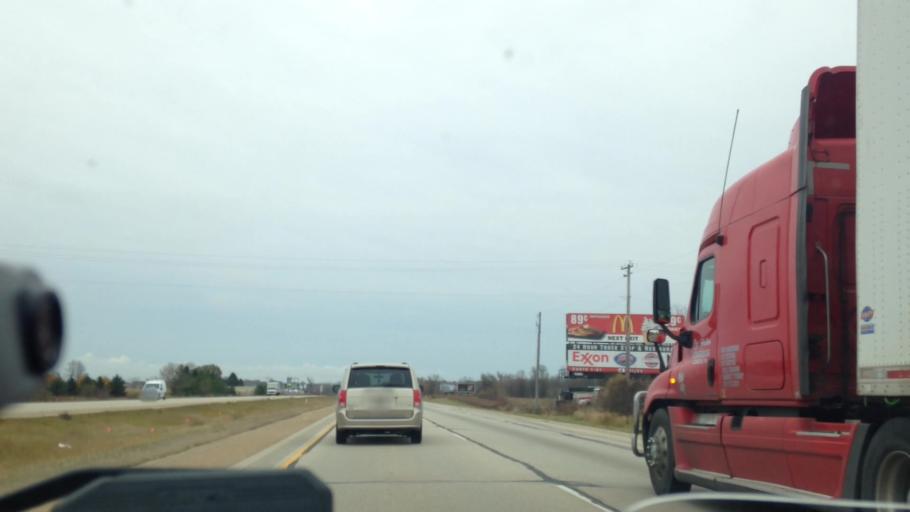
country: US
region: Wisconsin
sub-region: Washington County
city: Richfield
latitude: 43.3081
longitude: -88.2284
